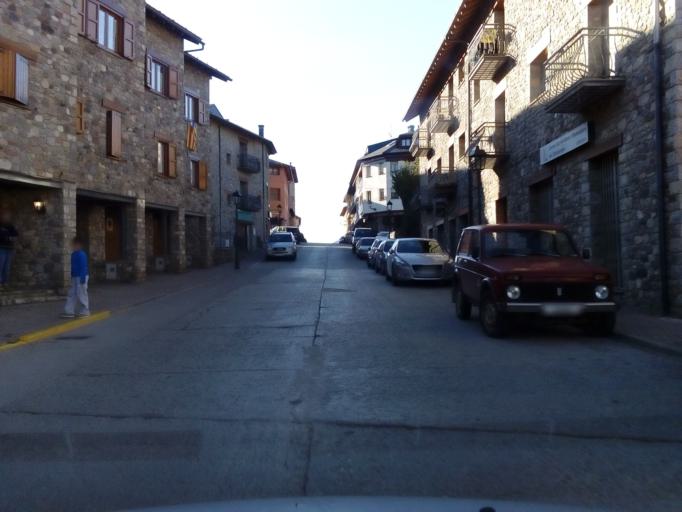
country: ES
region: Catalonia
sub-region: Provincia de Lleida
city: Bellver de Cerdanya
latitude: 42.3693
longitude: 1.7769
